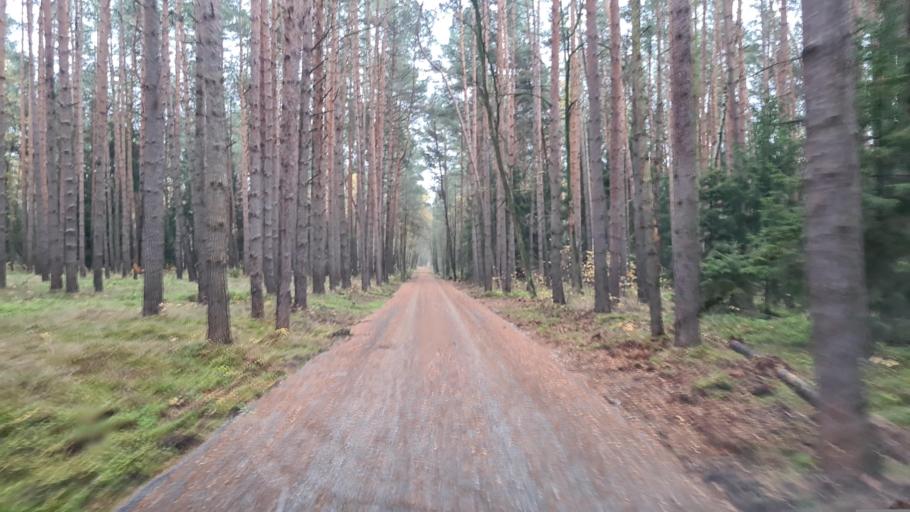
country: DE
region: Brandenburg
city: Kroppen
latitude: 51.4015
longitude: 13.7997
